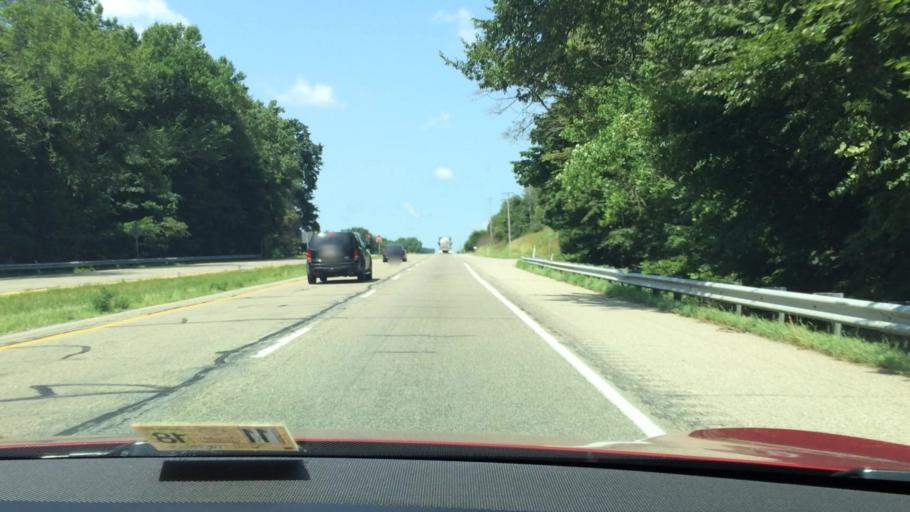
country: US
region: Indiana
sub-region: LaPorte County
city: Hudson Lake
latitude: 41.6726
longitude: -86.5444
